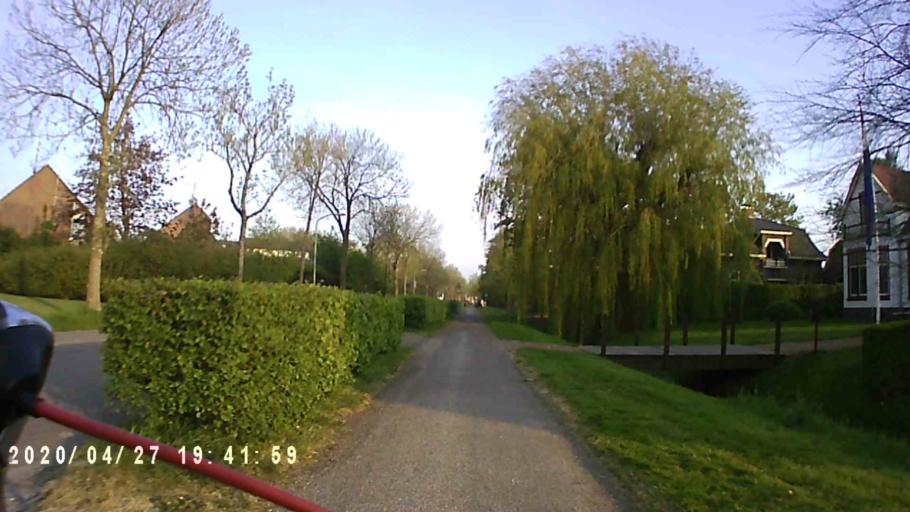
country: NL
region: Groningen
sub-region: Gemeente Winsum
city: Winsum
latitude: 53.3605
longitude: 6.4621
